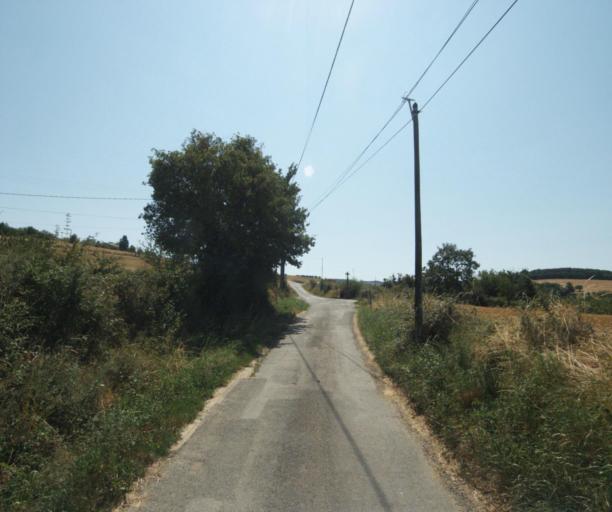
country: FR
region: Rhone-Alpes
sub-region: Departement du Rhone
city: Sain-Bel
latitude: 45.7959
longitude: 4.5972
